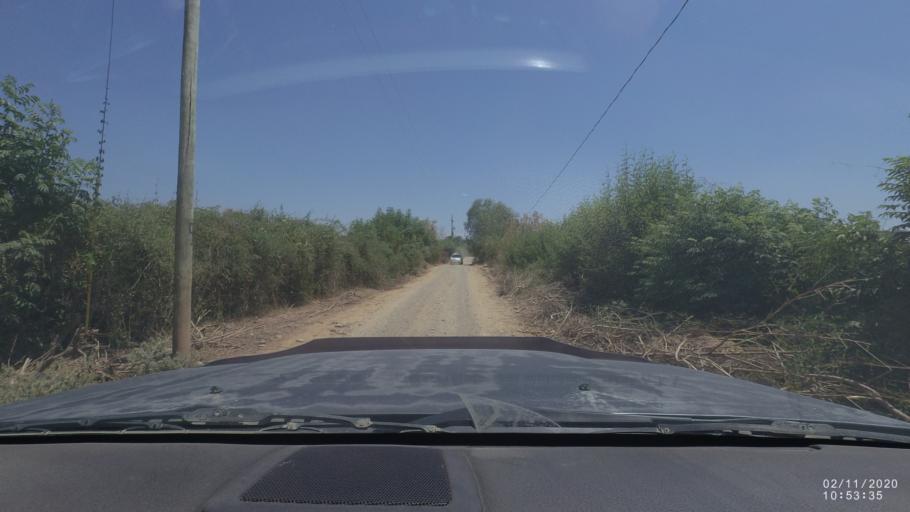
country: BO
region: Cochabamba
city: Aiquile
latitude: -18.1778
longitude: -64.8694
